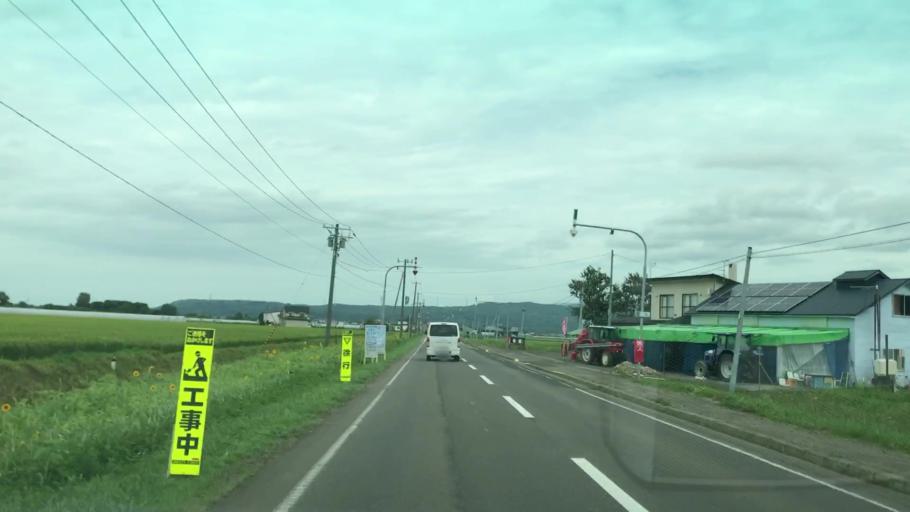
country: JP
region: Hokkaido
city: Iwanai
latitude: 43.0071
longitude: 140.5807
